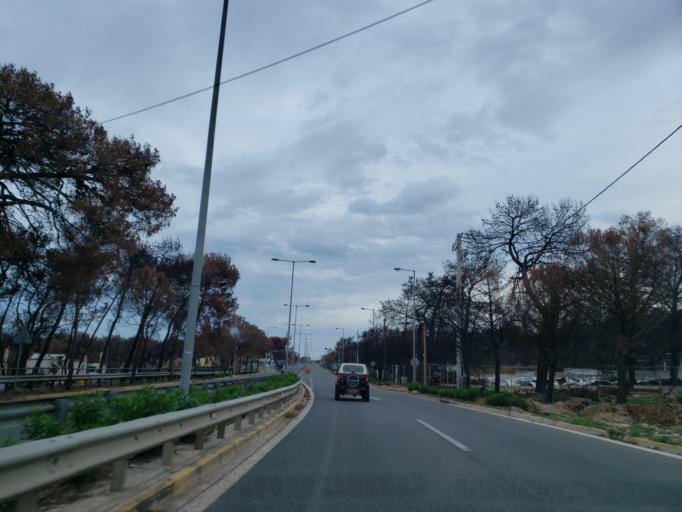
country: GR
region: Attica
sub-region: Nomarchia Anatolikis Attikis
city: Neos Voutzas
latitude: 38.0539
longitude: 23.9846
